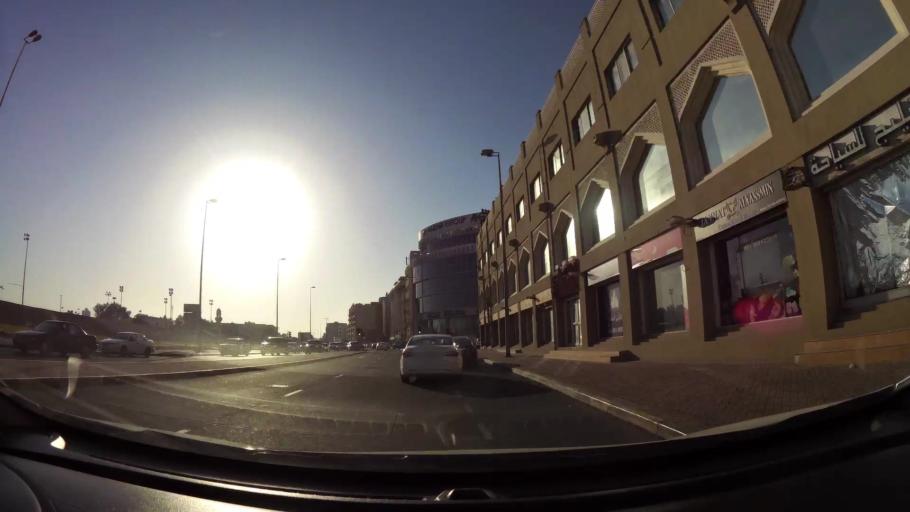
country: BH
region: Manama
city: Manama
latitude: 26.2242
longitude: 50.5972
